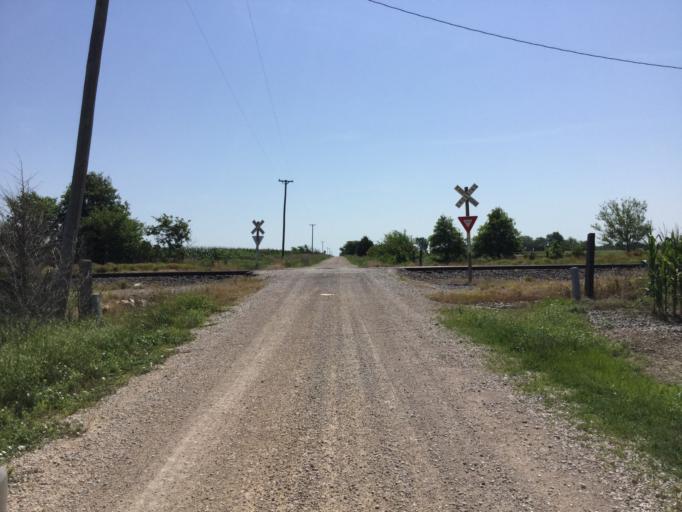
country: US
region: Kansas
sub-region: Woodson County
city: Yates Center
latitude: 37.8354
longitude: -95.6936
